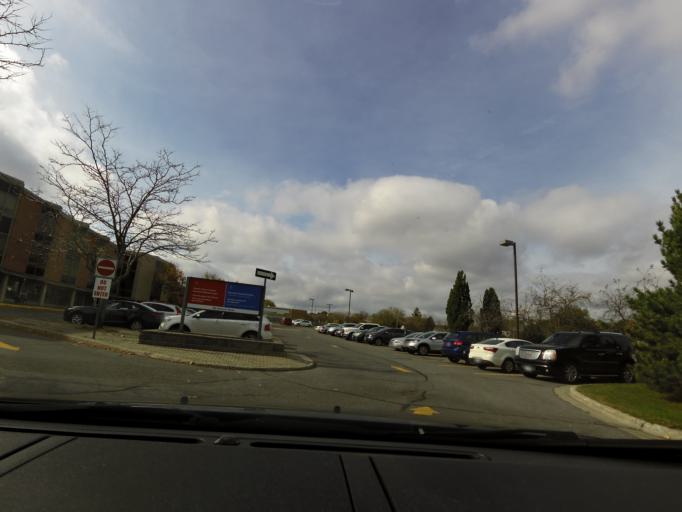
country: CA
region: Ontario
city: Kingston
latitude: 44.2416
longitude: -76.4878
